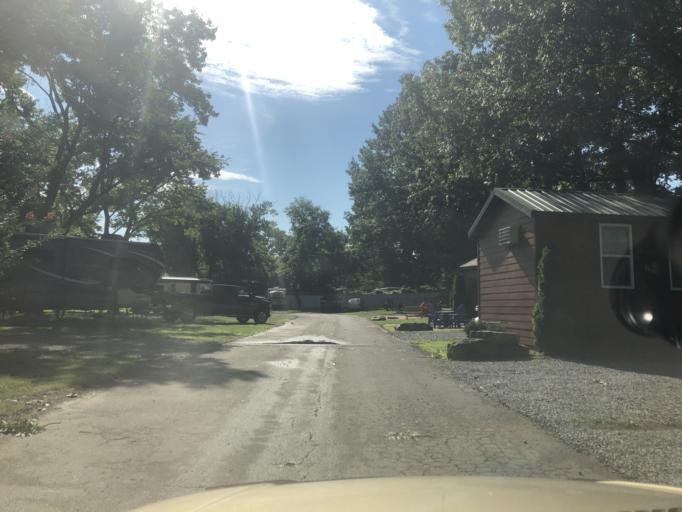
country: US
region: Tennessee
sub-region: Davidson County
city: Lakewood
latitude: 36.2325
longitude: -86.7061
